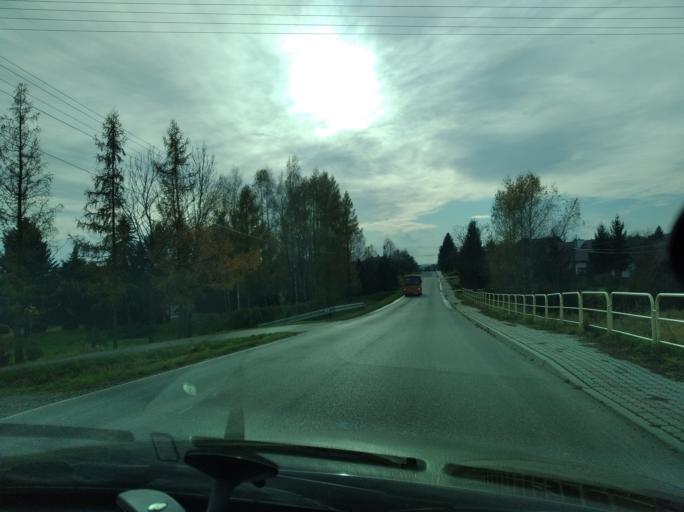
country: PL
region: Subcarpathian Voivodeship
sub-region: Powiat ropczycko-sedziszowski
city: Iwierzyce
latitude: 50.0250
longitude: 21.7559
